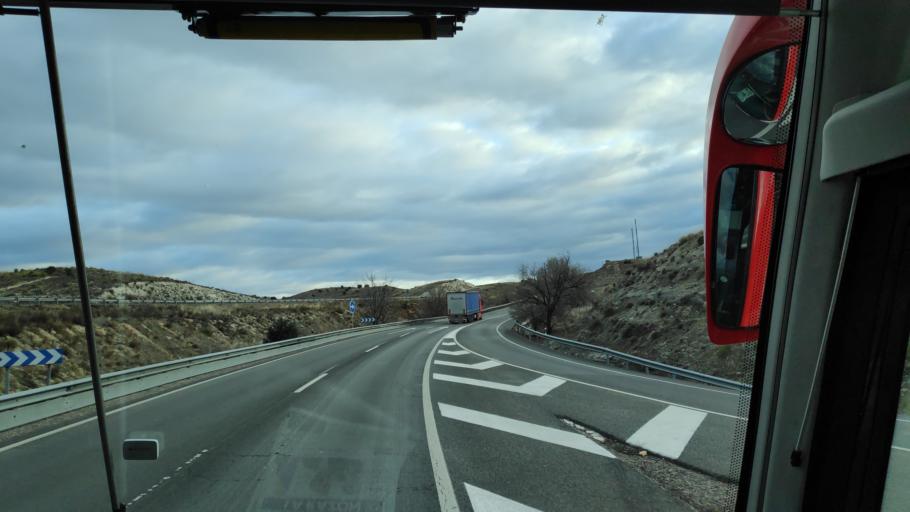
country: ES
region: Madrid
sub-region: Provincia de Madrid
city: Tielmes
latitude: 40.2064
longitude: -3.3150
